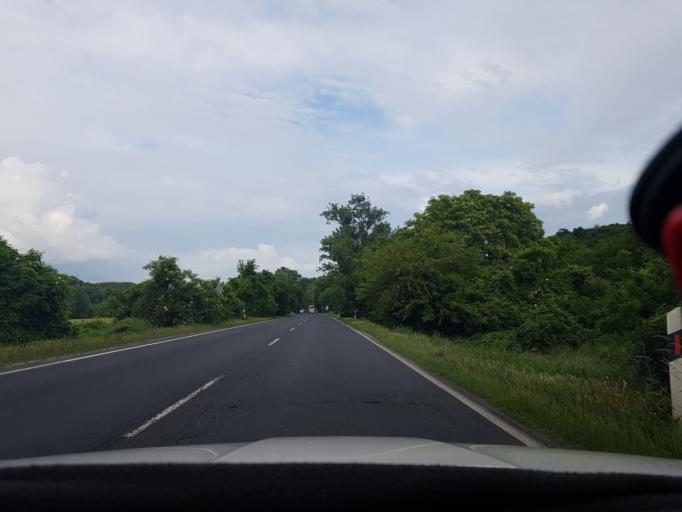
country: HU
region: Komarom-Esztergom
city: Neszmely
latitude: 47.7400
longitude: 18.3905
